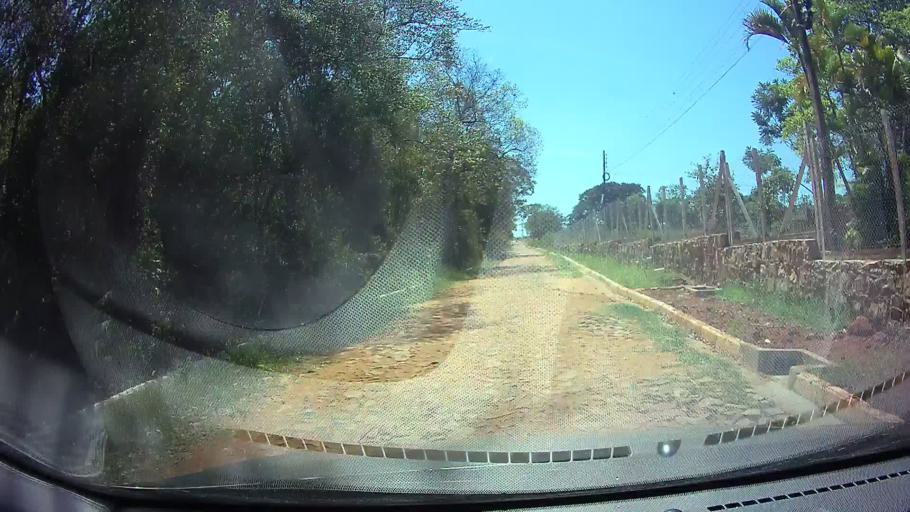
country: PY
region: Central
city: Limpio
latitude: -25.2326
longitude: -57.4376
